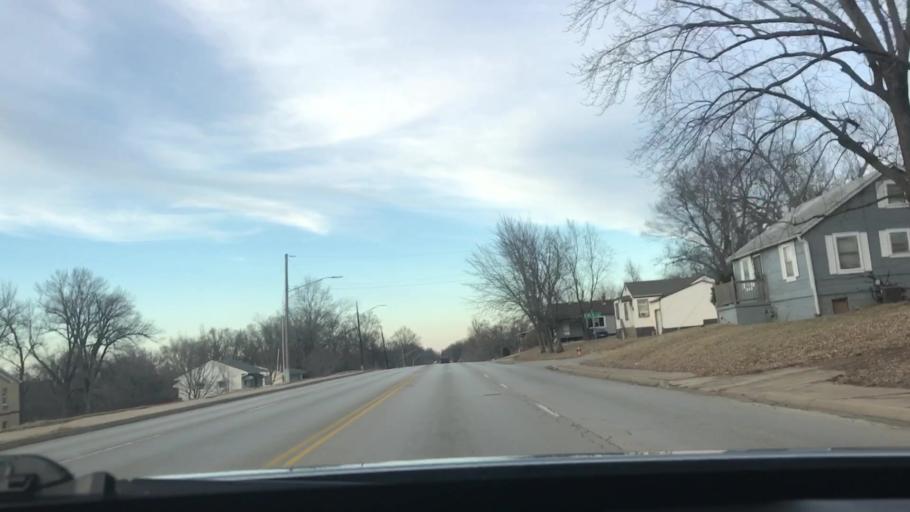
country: US
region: Missouri
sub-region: Jackson County
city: Independence
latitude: 39.0697
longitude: -94.4465
